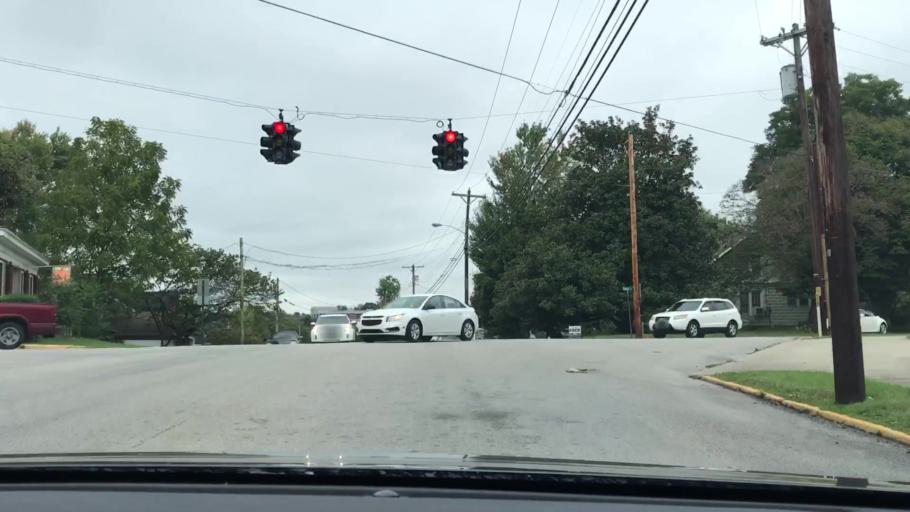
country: US
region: Kentucky
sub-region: Pulaski County
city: Somerset
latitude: 37.0884
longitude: -84.5996
